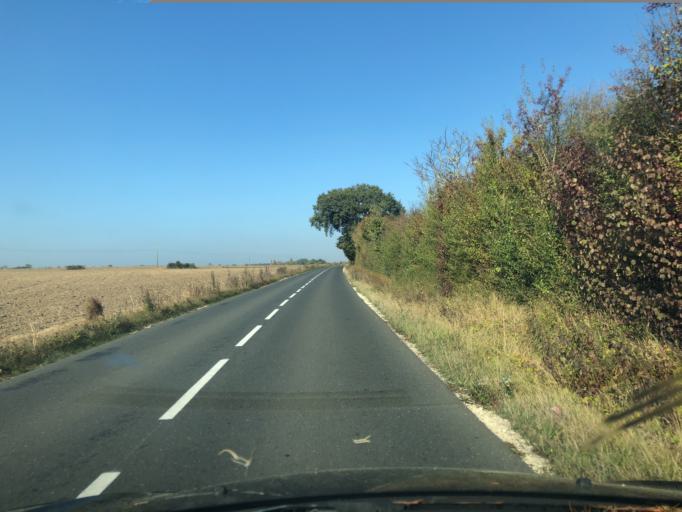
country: FR
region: Centre
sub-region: Departement d'Indre-et-Loire
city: Mettray
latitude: 47.4631
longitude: 0.6708
